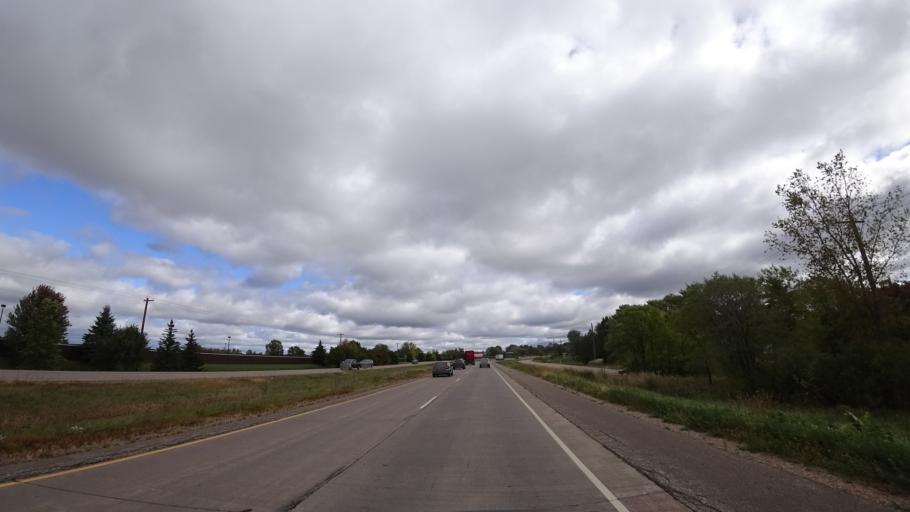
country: US
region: Wisconsin
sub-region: Eau Claire County
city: Eau Claire
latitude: 44.8435
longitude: -91.5628
